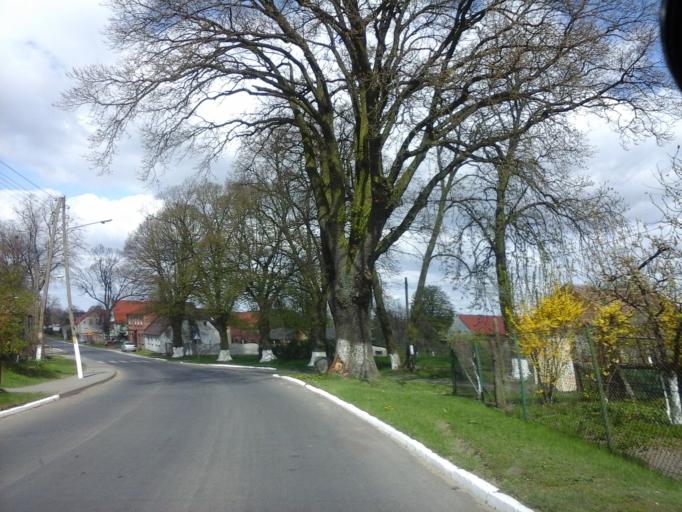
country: PL
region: West Pomeranian Voivodeship
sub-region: Powiat choszczenski
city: Recz
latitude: 53.1856
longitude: 15.5876
